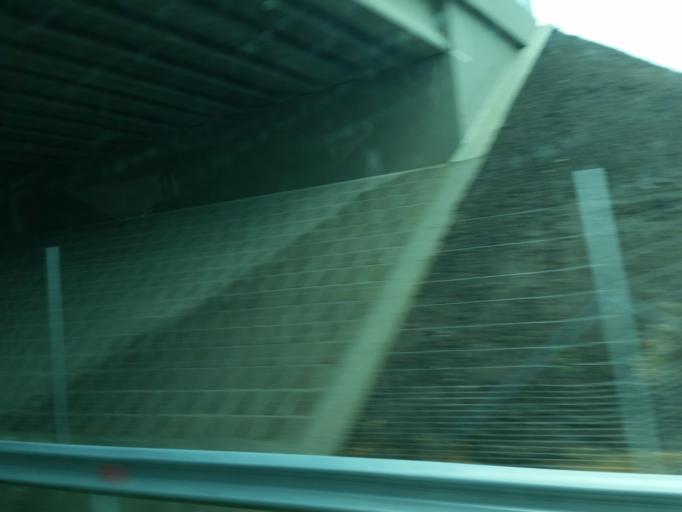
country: HU
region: Gyor-Moson-Sopron
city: Kony
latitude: 47.6388
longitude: 17.3499
